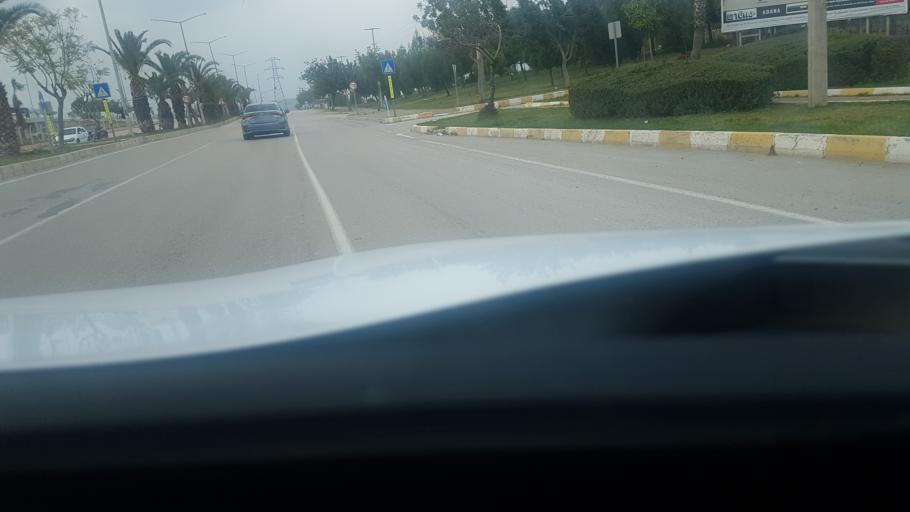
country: TR
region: Adana
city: Seyhan
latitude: 37.0559
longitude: 35.2478
